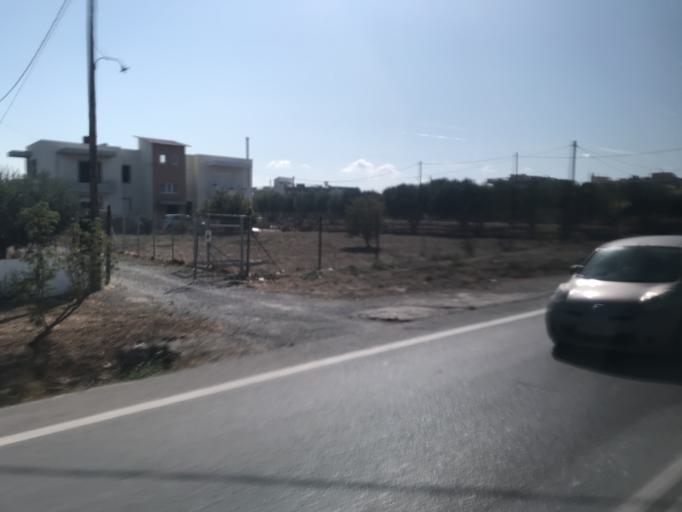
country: GR
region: Crete
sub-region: Nomos Irakleiou
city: Gazi
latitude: 35.3133
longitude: 25.0916
